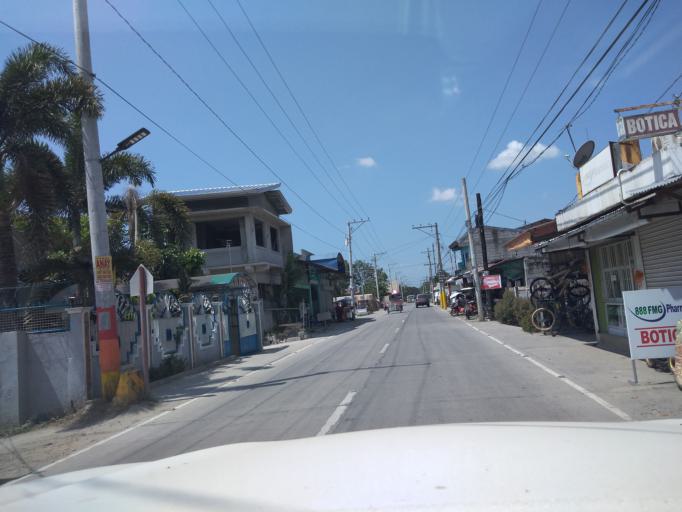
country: PH
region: Central Luzon
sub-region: Province of Pampanga
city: Lourdes
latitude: 15.0192
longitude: 120.8579
